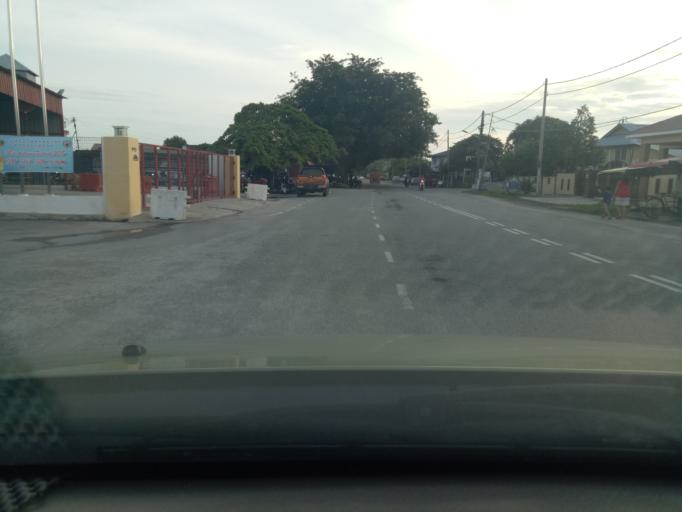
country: MY
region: Kedah
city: Alor Setar
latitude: 6.1232
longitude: 100.3567
